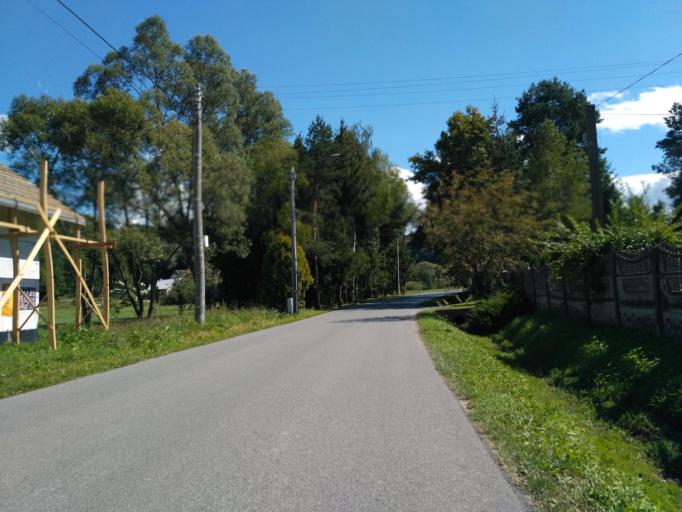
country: PL
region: Subcarpathian Voivodeship
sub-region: Powiat jasielski
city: Skolyszyn
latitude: 49.7976
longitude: 21.3186
